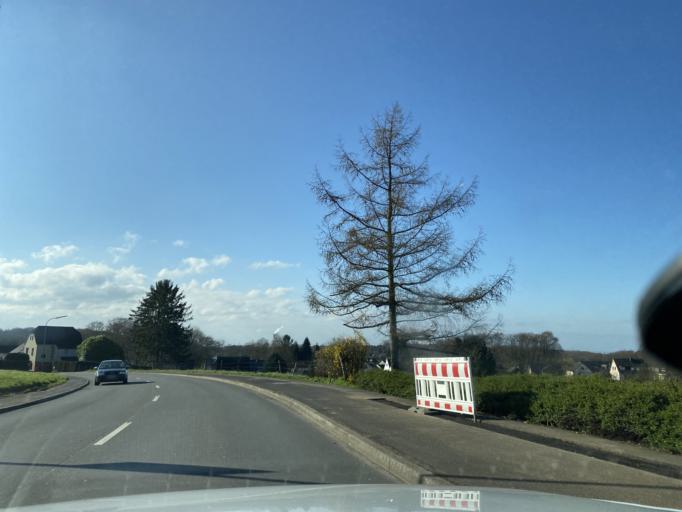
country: DE
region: North Rhine-Westphalia
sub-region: Regierungsbezirk Koln
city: Odenthal
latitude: 51.0155
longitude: 7.1244
